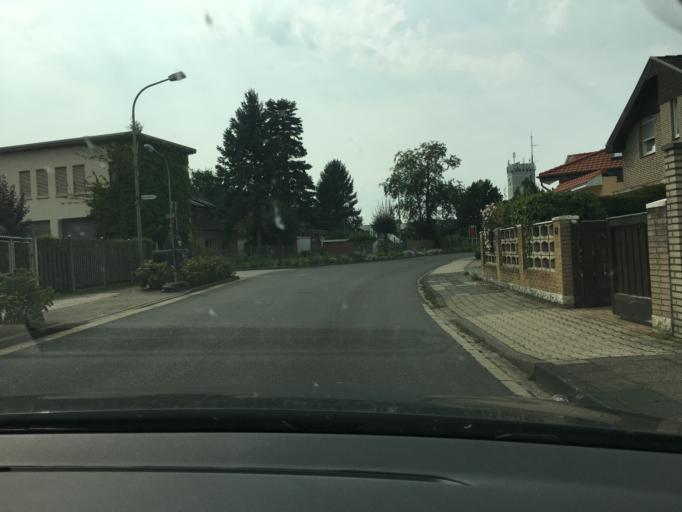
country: DE
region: North Rhine-Westphalia
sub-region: Regierungsbezirk Koln
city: Kreuzau
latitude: 50.7571
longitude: 6.5229
